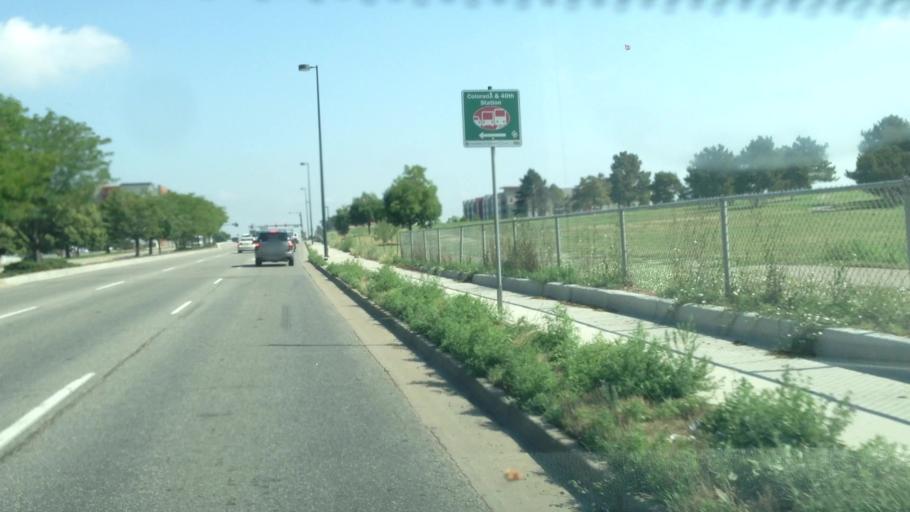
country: US
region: Colorado
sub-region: Adams County
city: Commerce City
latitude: 39.7698
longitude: -104.9404
